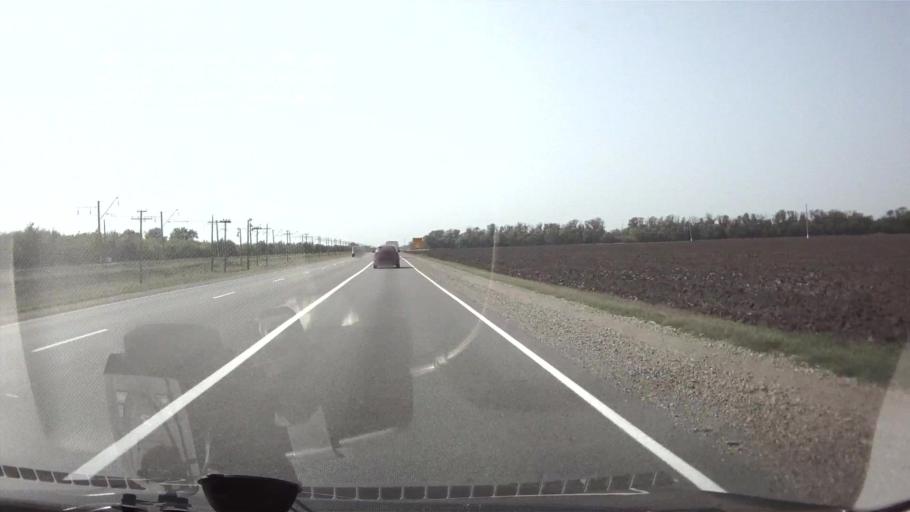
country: RU
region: Krasnodarskiy
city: Dvubratskiy
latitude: 45.2532
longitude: 39.7676
